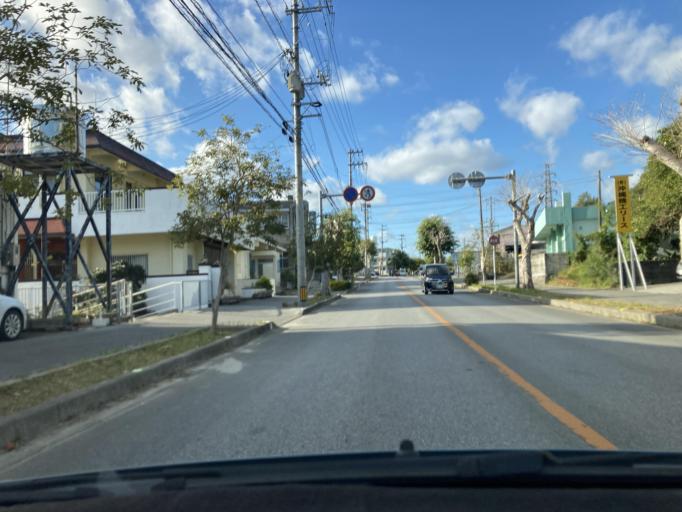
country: JP
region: Okinawa
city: Gushikawa
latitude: 26.3543
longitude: 127.8653
